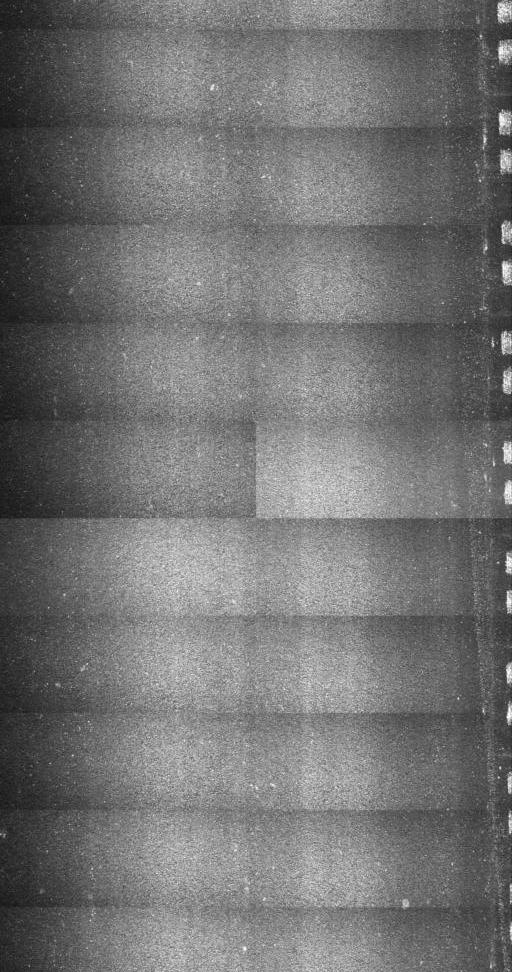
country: US
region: Vermont
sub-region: Franklin County
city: Richford
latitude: 44.9303
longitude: -72.6892
